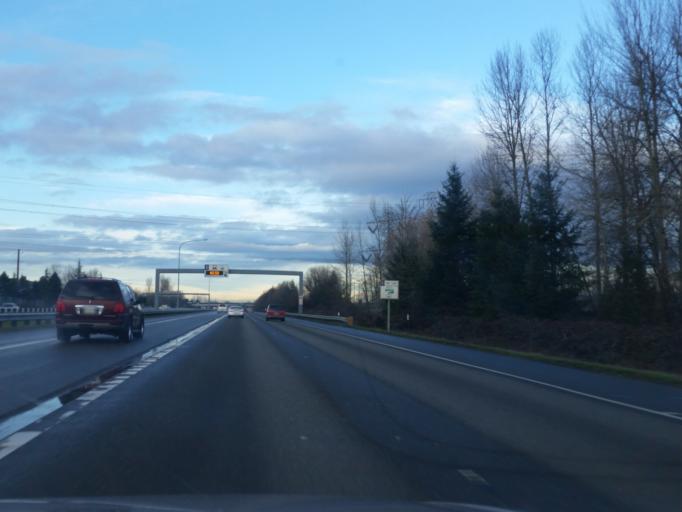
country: US
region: Washington
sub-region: King County
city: Auburn
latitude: 47.3332
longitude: -122.2447
